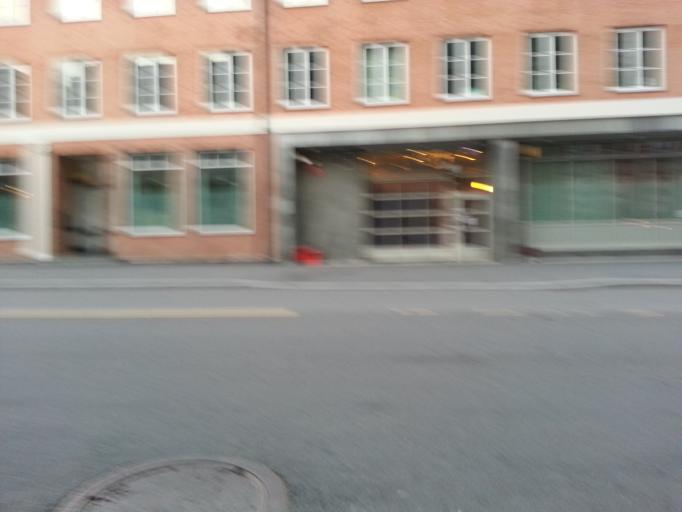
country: NO
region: Oslo
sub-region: Oslo
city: Oslo
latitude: 59.9084
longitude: 10.7455
